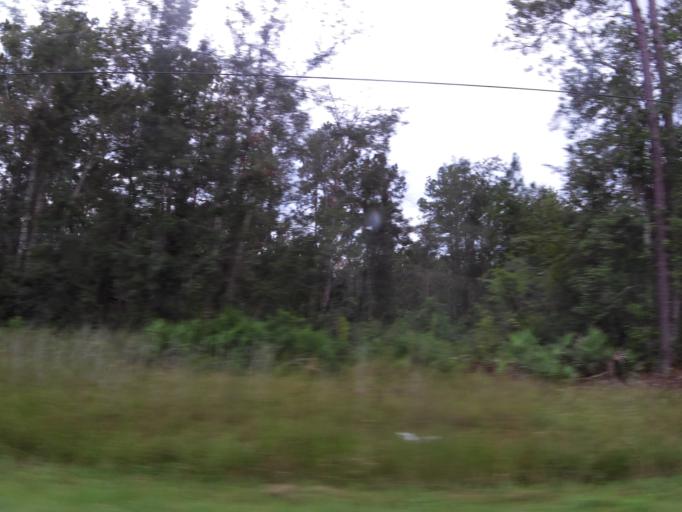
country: US
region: Florida
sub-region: Duval County
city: Baldwin
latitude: 30.4054
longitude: -82.0203
